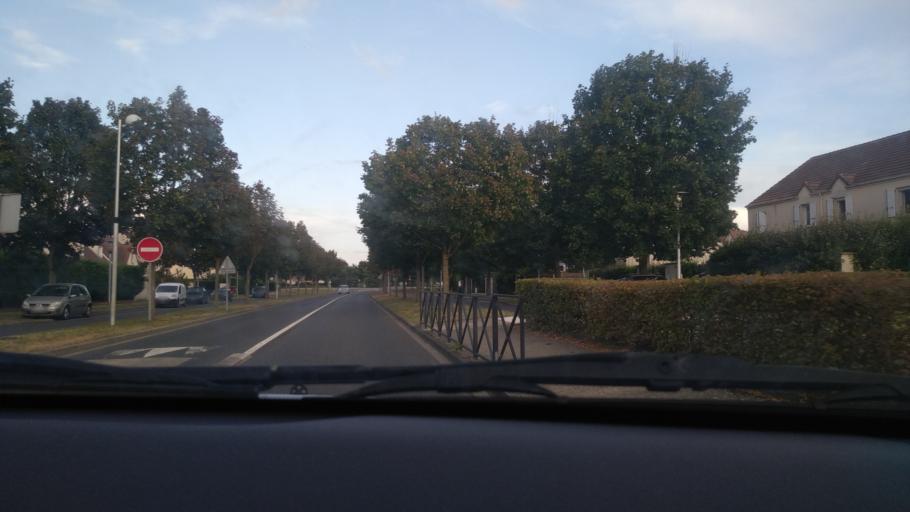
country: FR
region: Ile-de-France
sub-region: Departement de Seine-et-Marne
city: Lieusaint
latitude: 48.6369
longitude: 2.5535
